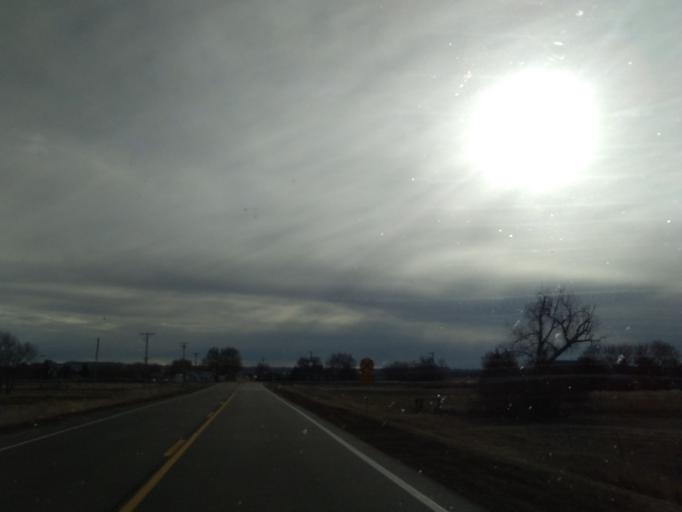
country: US
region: Nebraska
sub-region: Scotts Bluff County
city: Gering
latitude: 41.7868
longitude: -103.5191
